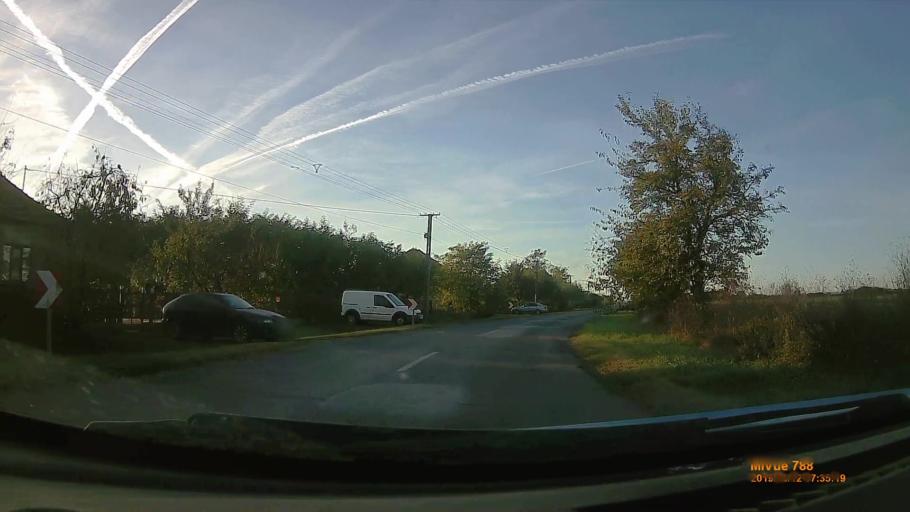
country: HU
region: Hajdu-Bihar
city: Pocsaj
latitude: 47.2547
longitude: 21.8112
